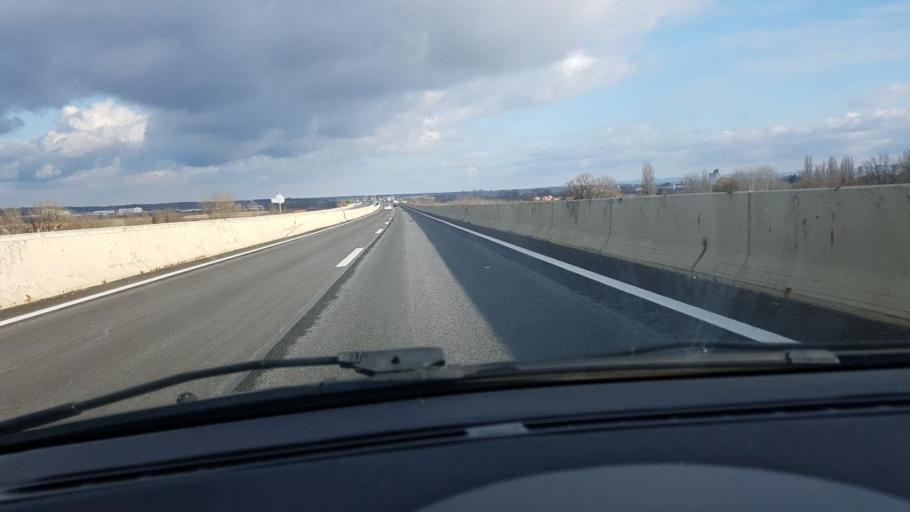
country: HR
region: Karlovacka
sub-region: Grad Karlovac
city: Karlovac
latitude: 45.5105
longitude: 15.5232
